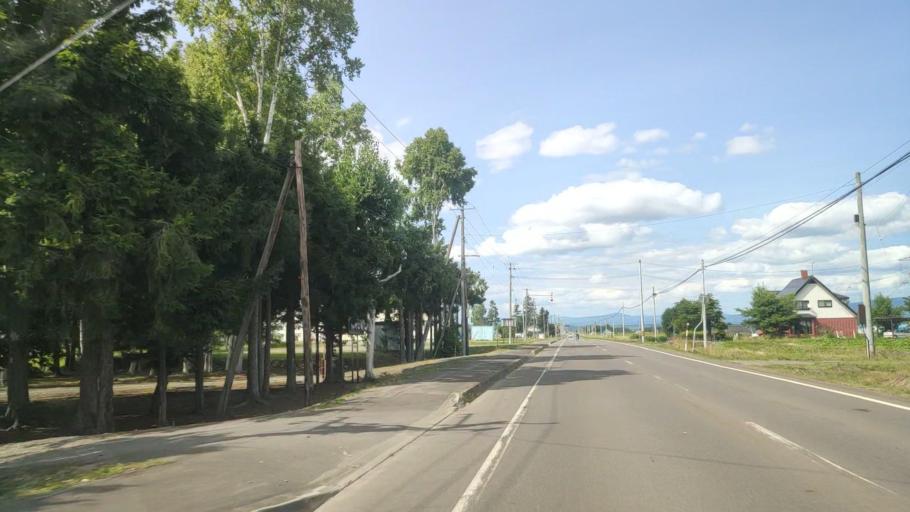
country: JP
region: Hokkaido
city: Nayoro
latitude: 44.2885
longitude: 142.4294
